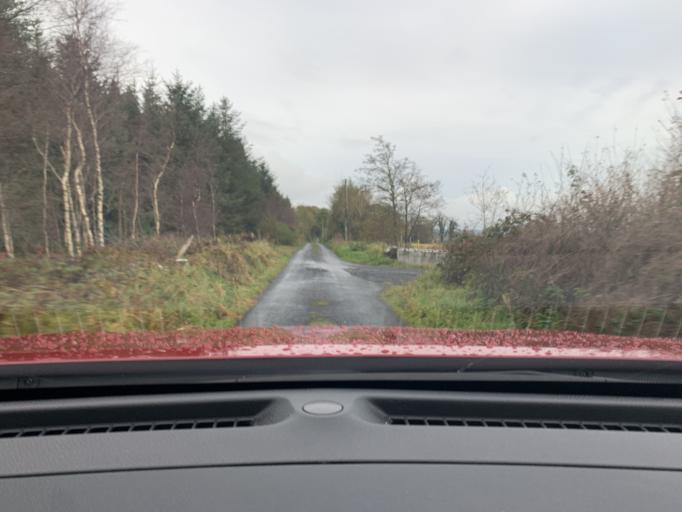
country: IE
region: Connaught
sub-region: Roscommon
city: Ballaghaderreen
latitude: 53.9193
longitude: -8.5580
